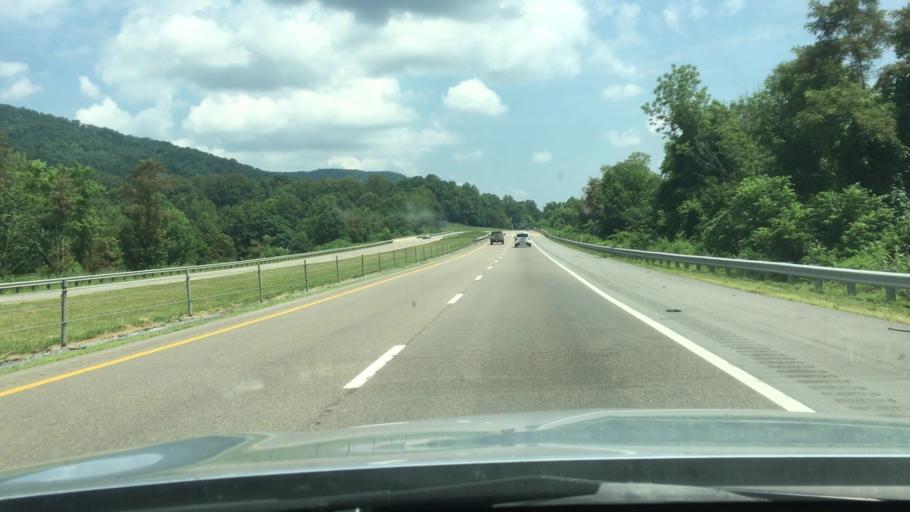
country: US
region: Tennessee
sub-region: Unicoi County
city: Unicoi
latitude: 36.2251
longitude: -82.3409
